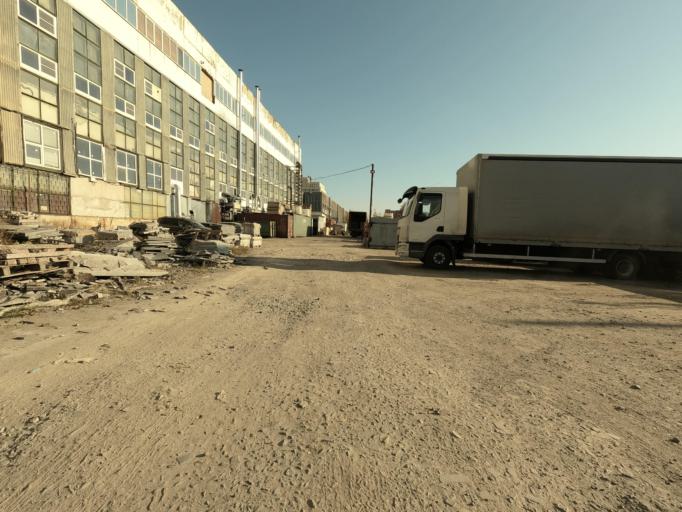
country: RU
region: St.-Petersburg
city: Obukhovo
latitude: 59.8423
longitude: 30.4732
